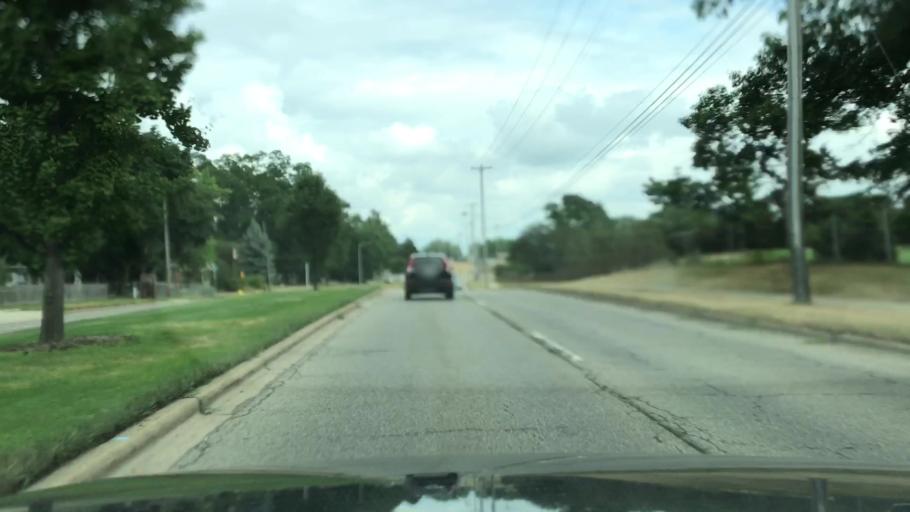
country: US
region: Michigan
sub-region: Kent County
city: Wyoming
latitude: 42.8843
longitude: -85.6986
